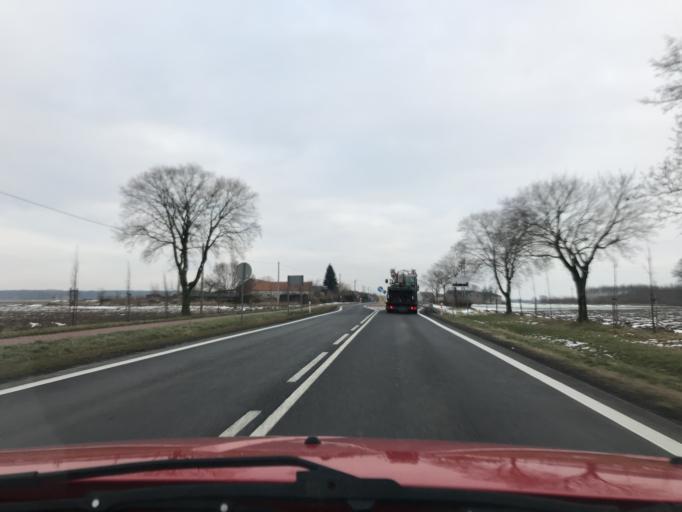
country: PL
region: Greater Poland Voivodeship
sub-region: Powiat pleszewski
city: Goluchow
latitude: 51.8723
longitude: 17.8921
